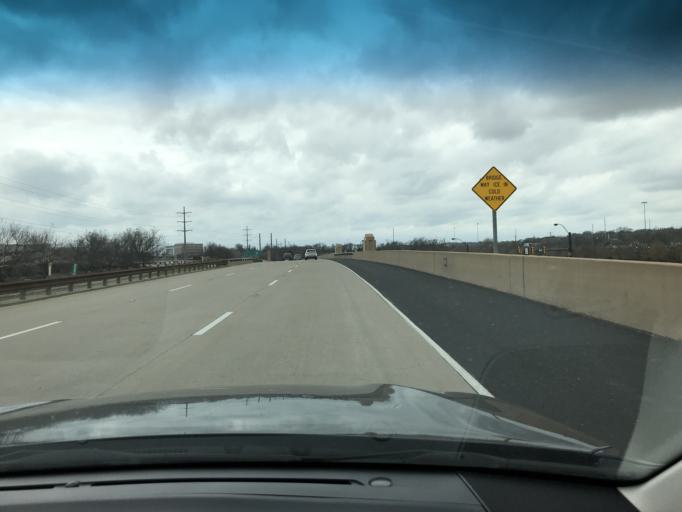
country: US
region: Texas
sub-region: Tarrant County
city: Westworth
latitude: 32.7133
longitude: -97.3977
